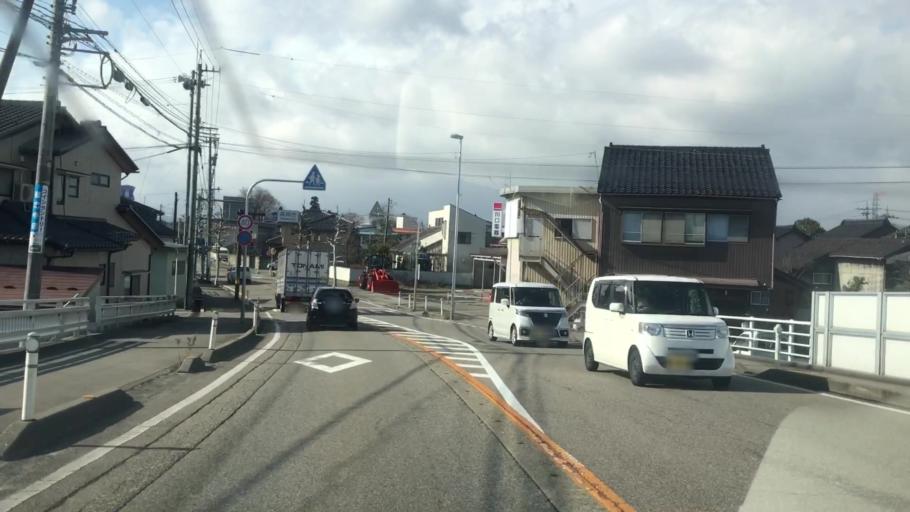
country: JP
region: Toyama
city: Takaoka
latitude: 36.7362
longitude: 137.0400
